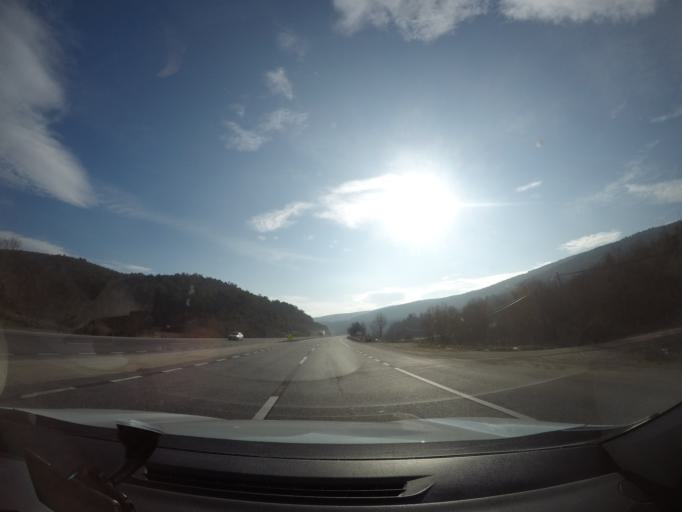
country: TR
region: Bilecik
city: Dodurga
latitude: 39.8898
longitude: 29.9235
